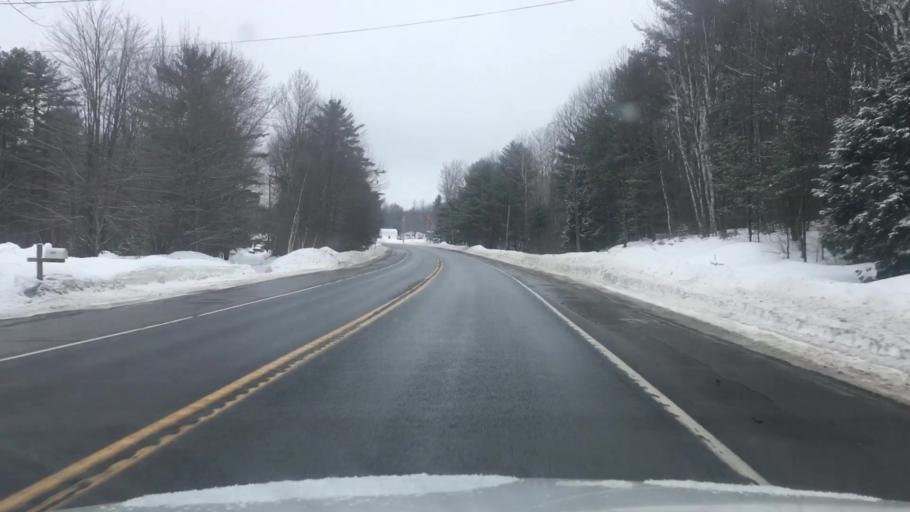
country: US
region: Maine
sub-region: Franklin County
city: New Sharon
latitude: 44.6526
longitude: -69.9611
